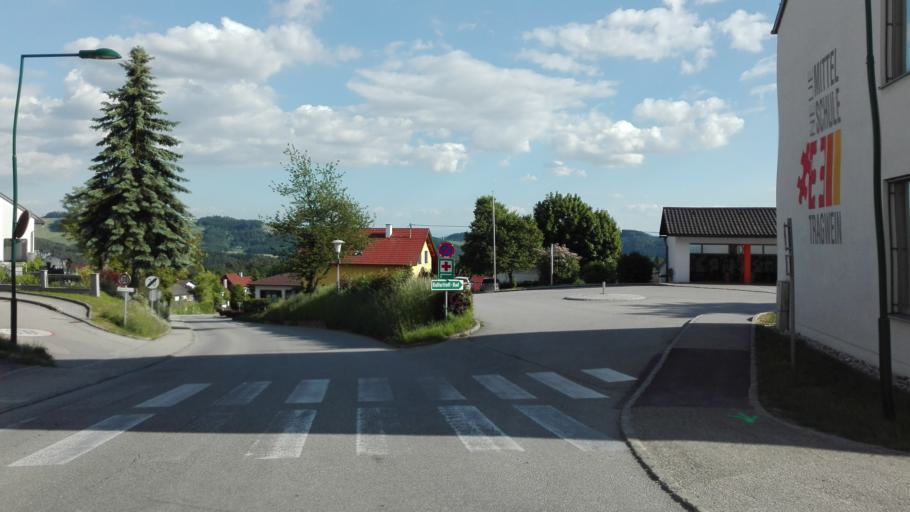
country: AT
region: Upper Austria
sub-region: Politischer Bezirk Perg
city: Perg
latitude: 48.3296
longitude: 14.6221
